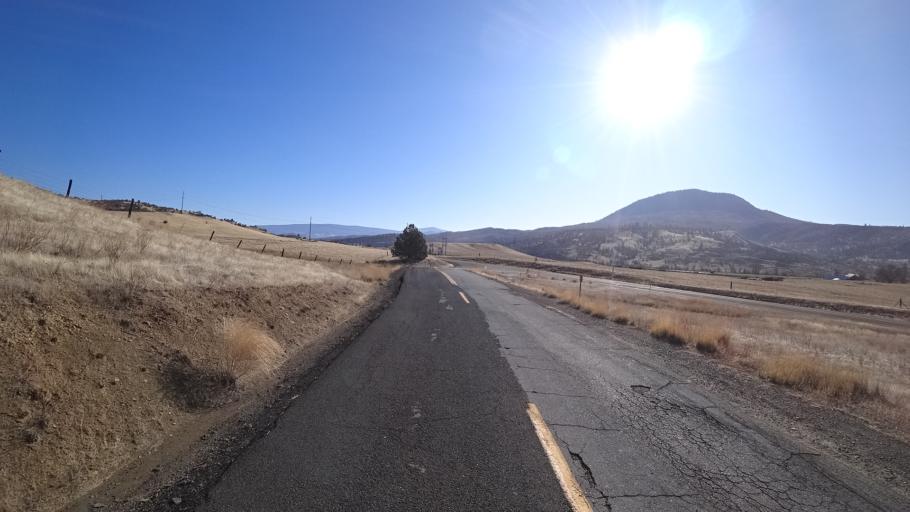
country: US
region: California
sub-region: Siskiyou County
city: Montague
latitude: 41.8987
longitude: -122.5424
